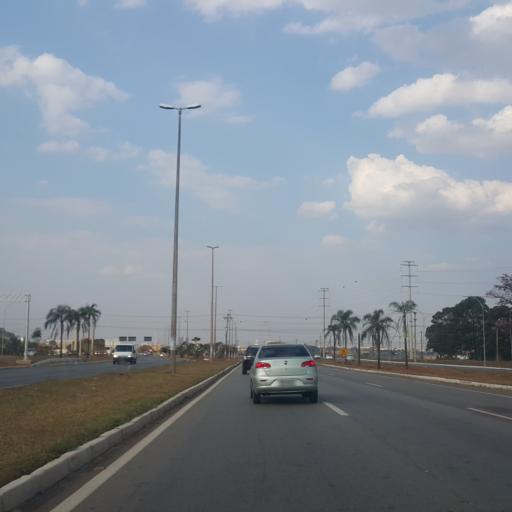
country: BR
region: Federal District
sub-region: Brasilia
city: Brasilia
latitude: -15.8823
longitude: -48.0596
